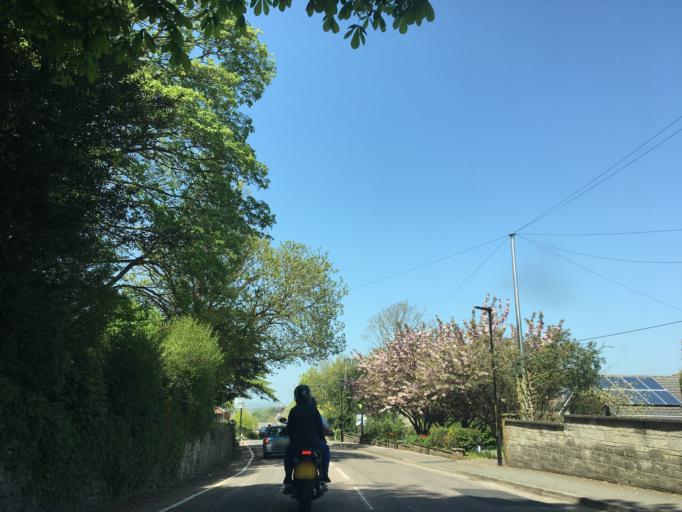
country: GB
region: England
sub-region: Isle of Wight
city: Niton
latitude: 50.5969
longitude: -1.2635
